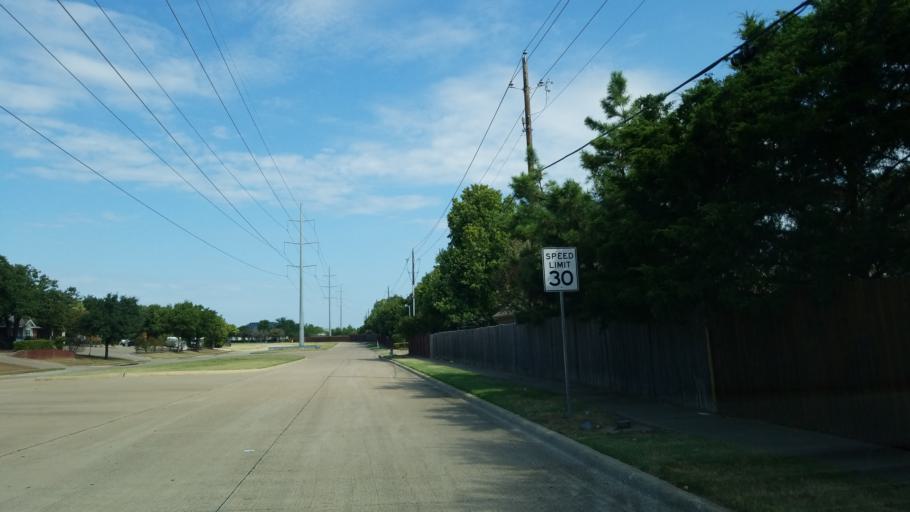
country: US
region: Texas
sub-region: Tarrant County
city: Euless
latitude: 32.8815
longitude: -97.0951
